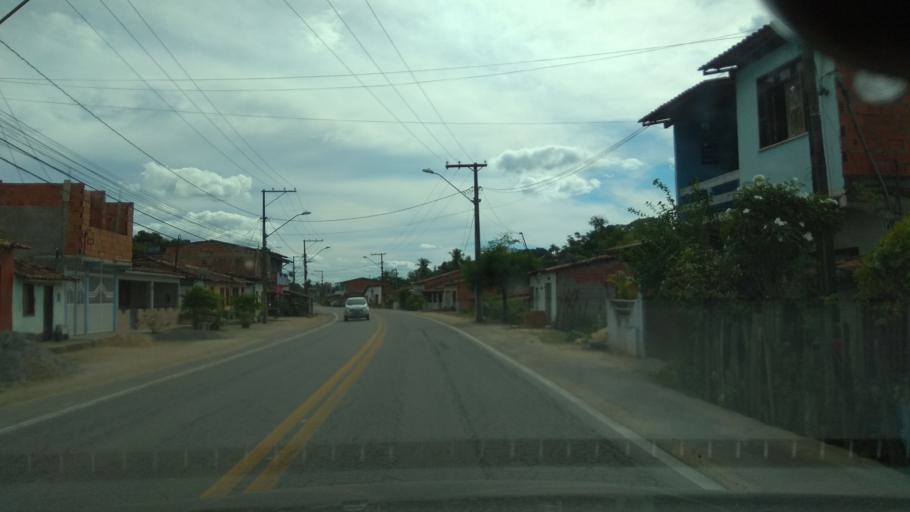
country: BR
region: Bahia
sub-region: Ipiau
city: Ipiau
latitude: -14.1255
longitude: -39.7598
